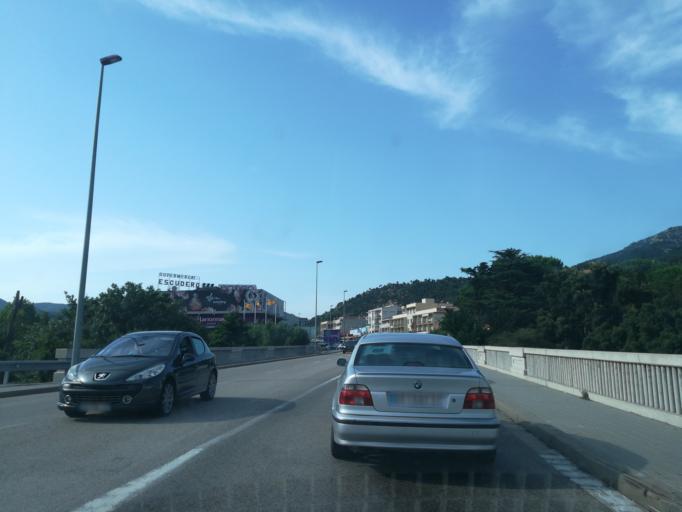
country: ES
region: Catalonia
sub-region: Provincia de Girona
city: la Jonquera
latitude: 42.4263
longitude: 2.8684
